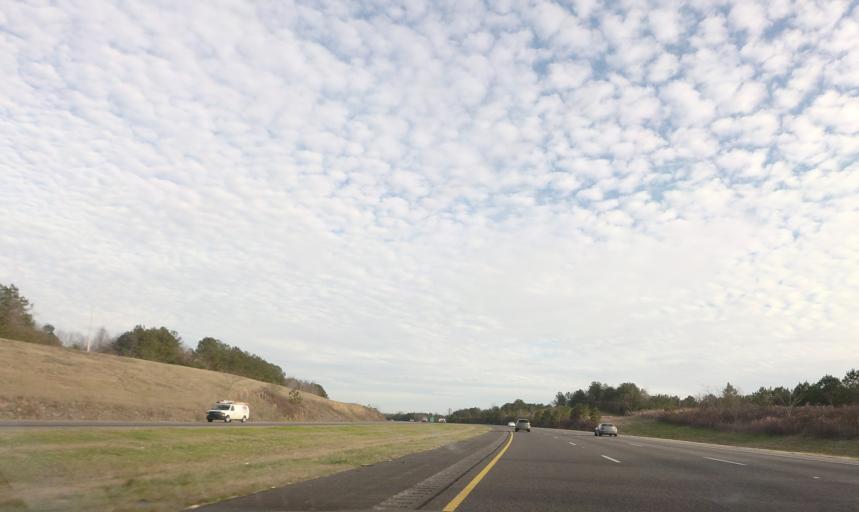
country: US
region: Alabama
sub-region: Walker County
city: Dora
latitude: 33.6663
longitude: -87.0688
